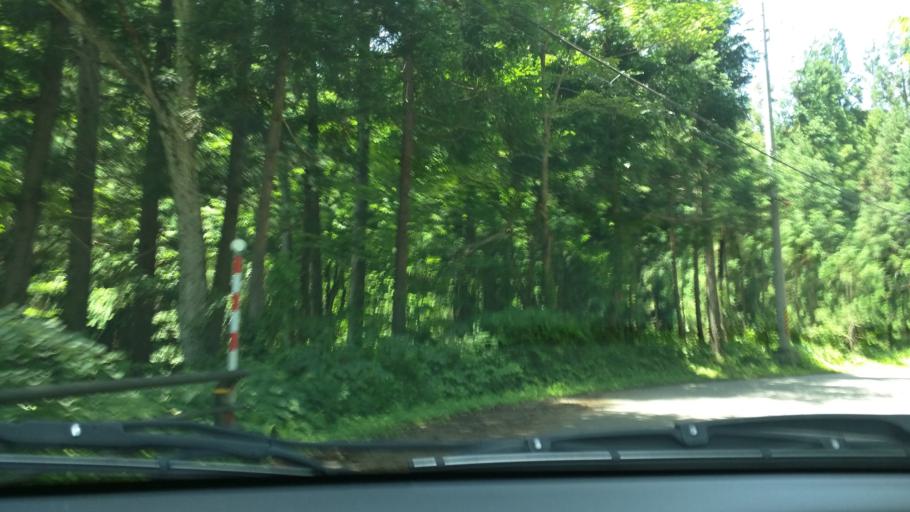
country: JP
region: Tochigi
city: Kuroiso
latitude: 37.2564
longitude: 139.7848
